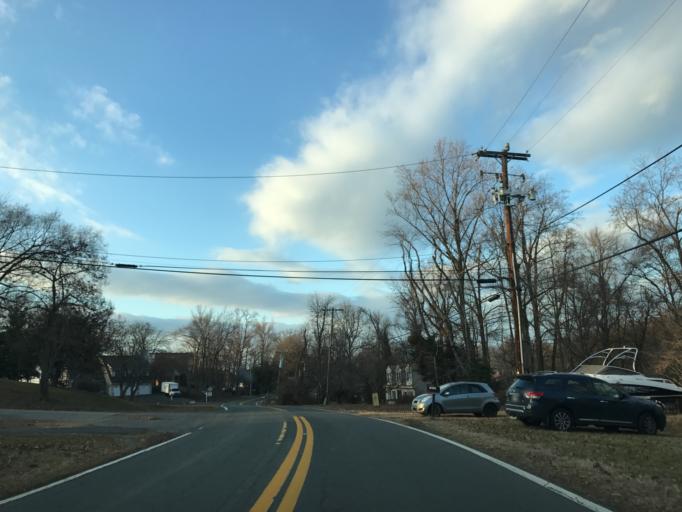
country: US
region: Maryland
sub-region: Cecil County
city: Charlestown
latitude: 39.4647
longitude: -75.9953
